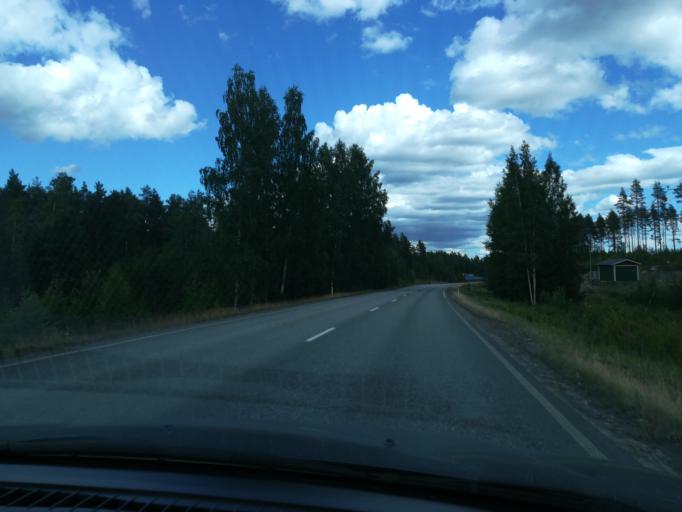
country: FI
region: Southern Savonia
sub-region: Mikkeli
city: Hirvensalmi
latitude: 61.6705
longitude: 26.8288
